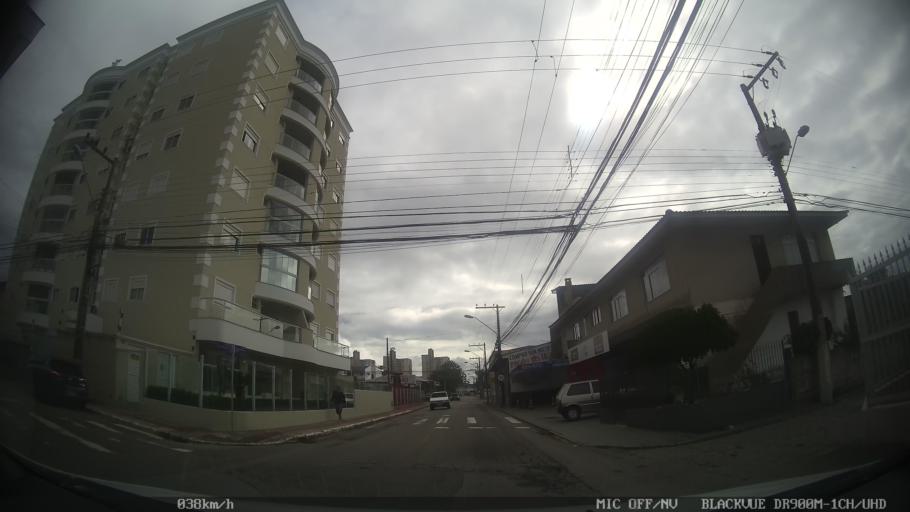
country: BR
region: Santa Catarina
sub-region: Sao Jose
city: Campinas
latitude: -27.5592
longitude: -48.6210
